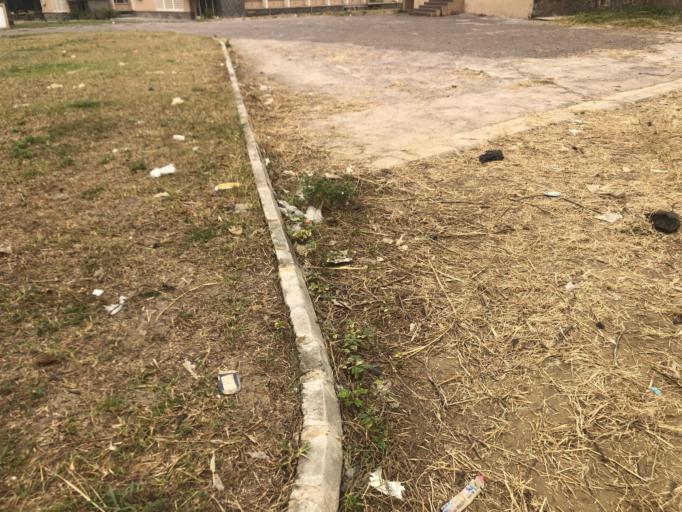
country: CD
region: Kinshasa
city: Masina
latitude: -4.4252
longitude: 15.3099
